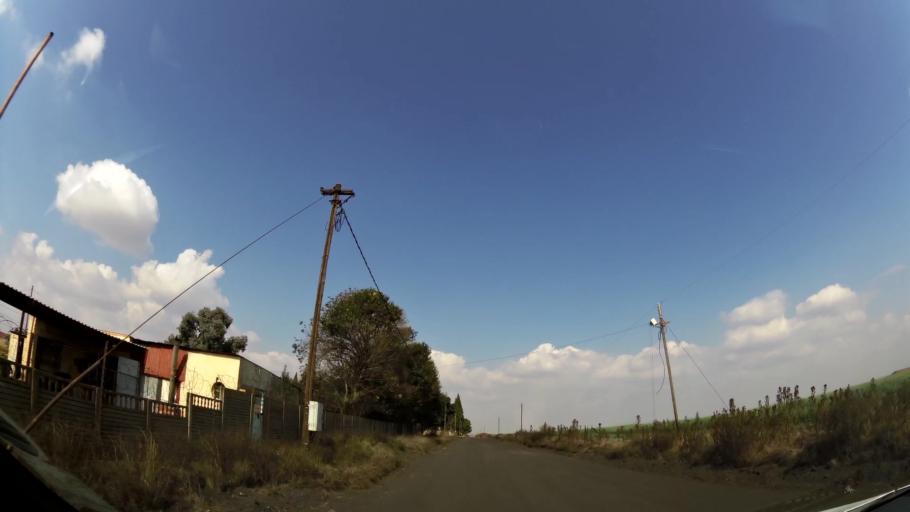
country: ZA
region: Gauteng
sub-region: Ekurhuleni Metropolitan Municipality
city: Springs
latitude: -26.1880
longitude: 28.5333
